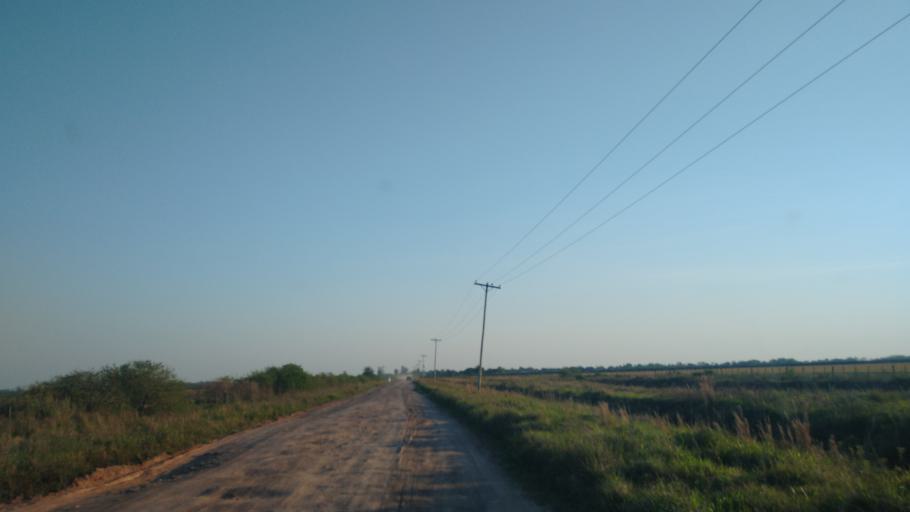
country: PY
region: Neembucu
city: Cerrito
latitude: -27.3864
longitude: -57.6576
